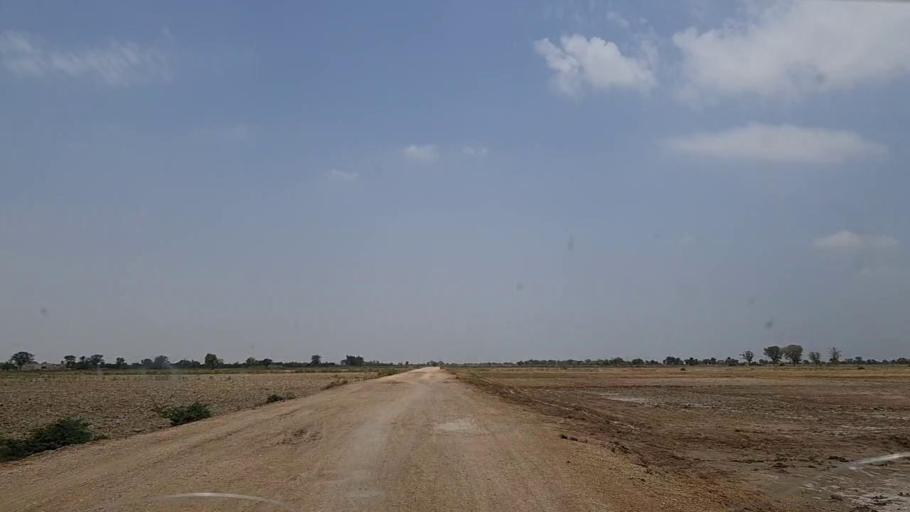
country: PK
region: Sindh
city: Phulji
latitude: 26.8125
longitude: 67.6340
